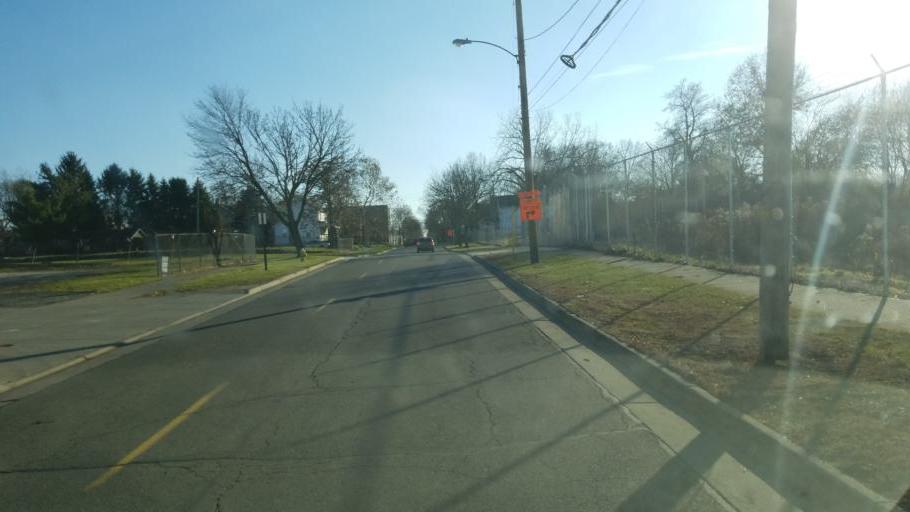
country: US
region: Ohio
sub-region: Summit County
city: Akron
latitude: 41.0577
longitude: -81.5195
